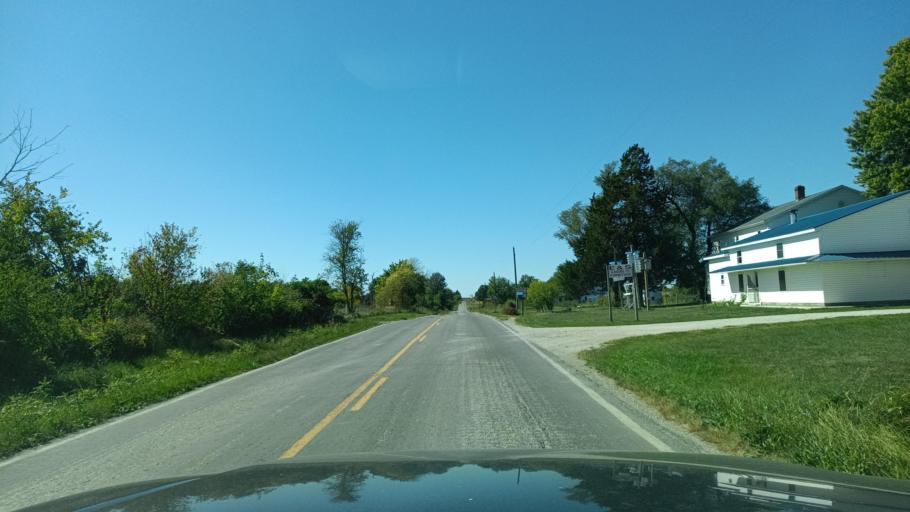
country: US
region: Missouri
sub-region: Macon County
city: La Plata
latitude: 40.0222
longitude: -92.5533
